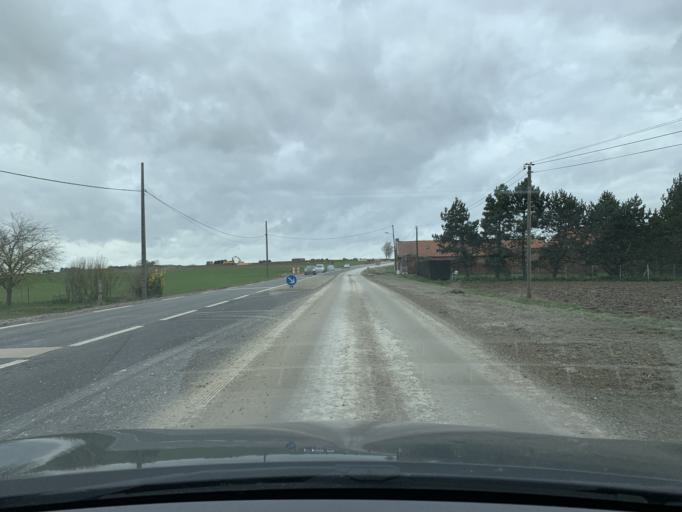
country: FR
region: Nord-Pas-de-Calais
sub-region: Departement du Nord
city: Raillencourt-Sainte-Olle
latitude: 50.2137
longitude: 3.1843
